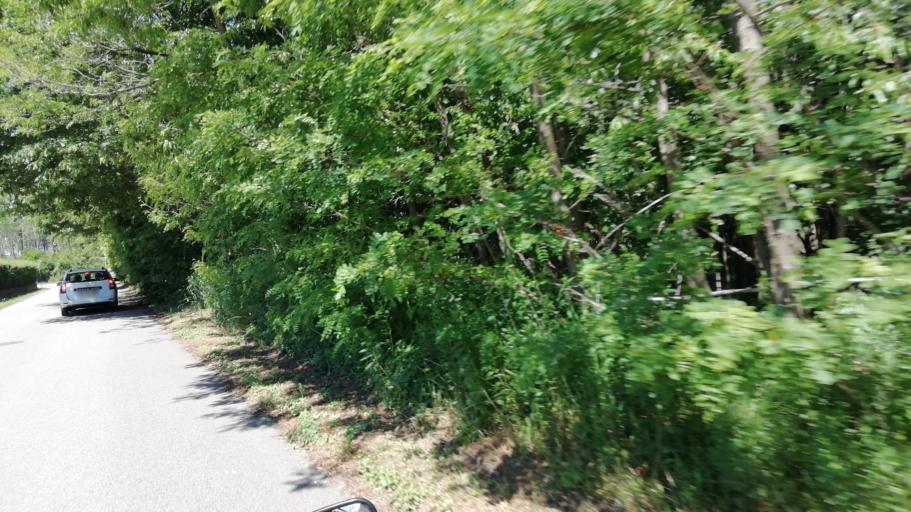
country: IT
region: Lombardy
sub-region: Provincia di Varese
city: Ferno
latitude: 45.6269
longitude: 8.7478
